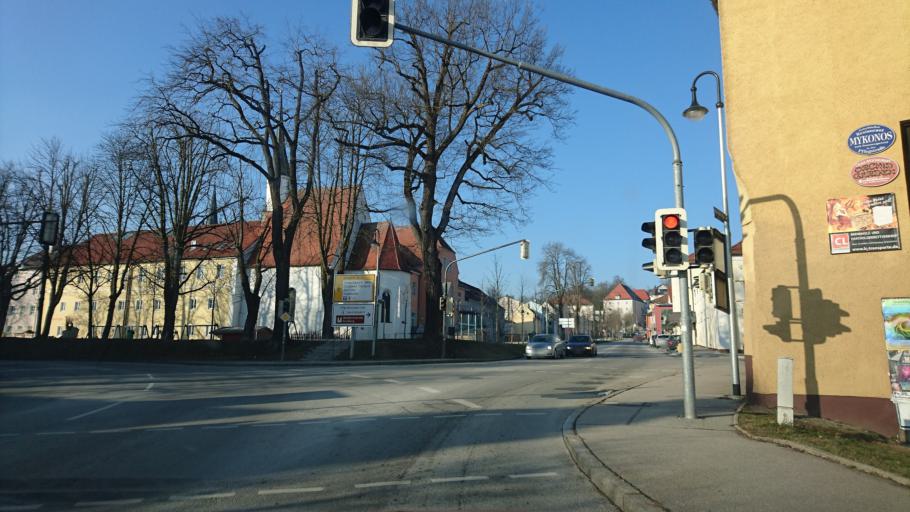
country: DE
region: Bavaria
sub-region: Lower Bavaria
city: Pfarrkirchen
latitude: 48.4306
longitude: 12.9418
